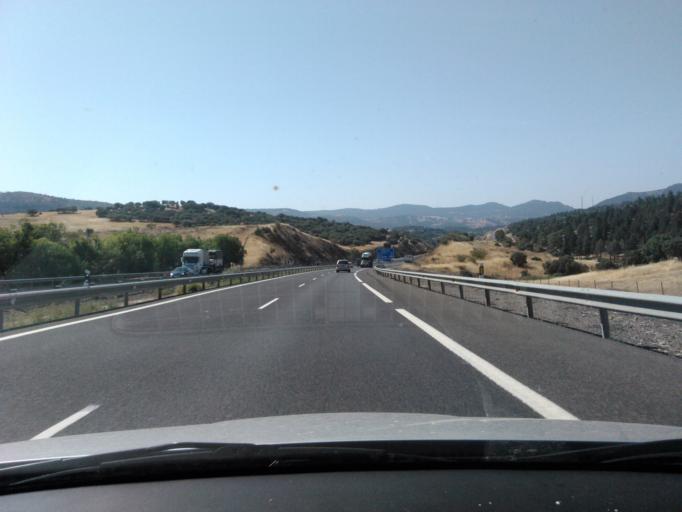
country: ES
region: Castille-La Mancha
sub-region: Provincia de Ciudad Real
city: Viso del Marques
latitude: 38.4544
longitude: -3.4978
